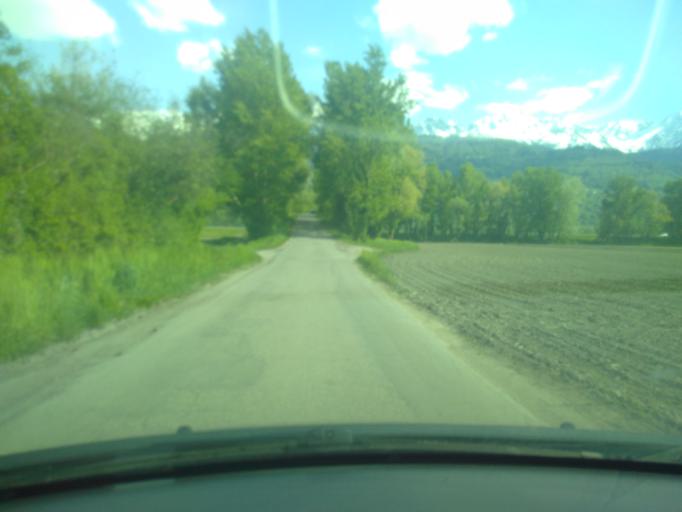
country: FR
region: Rhone-Alpes
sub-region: Departement de l'Isere
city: Froges
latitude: 45.2835
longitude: 5.9079
